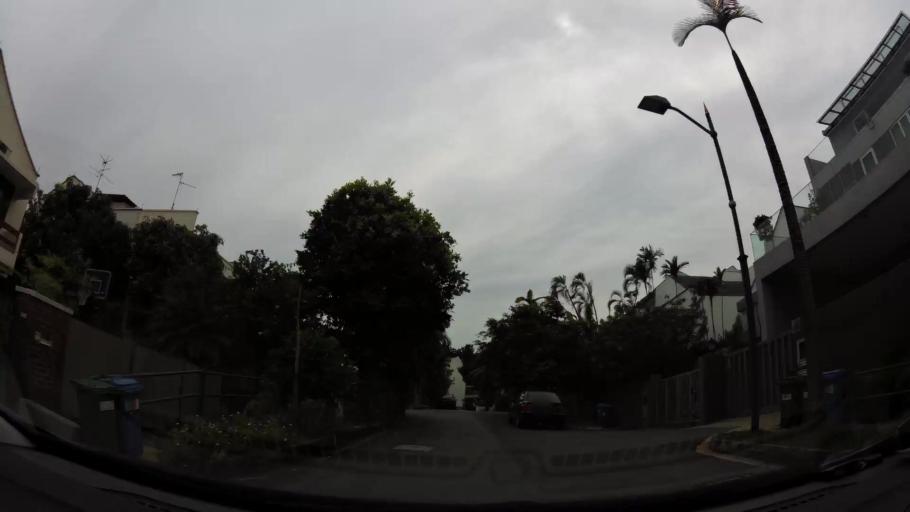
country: SG
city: Singapore
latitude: 1.3607
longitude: 103.8650
